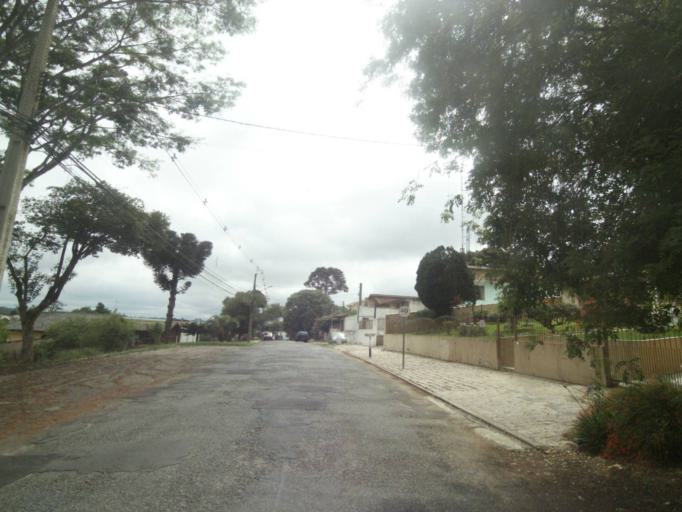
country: BR
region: Parana
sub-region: Curitiba
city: Curitiba
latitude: -25.3937
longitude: -49.2811
